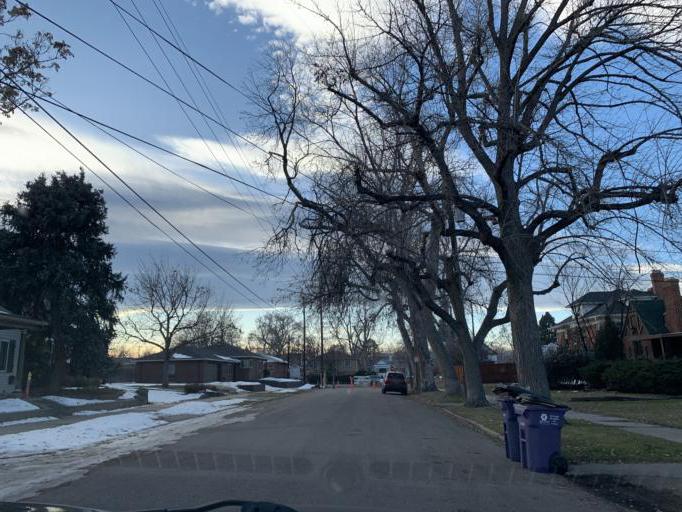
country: US
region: Colorado
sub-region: Adams County
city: Berkley
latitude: 39.7792
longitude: -105.0335
